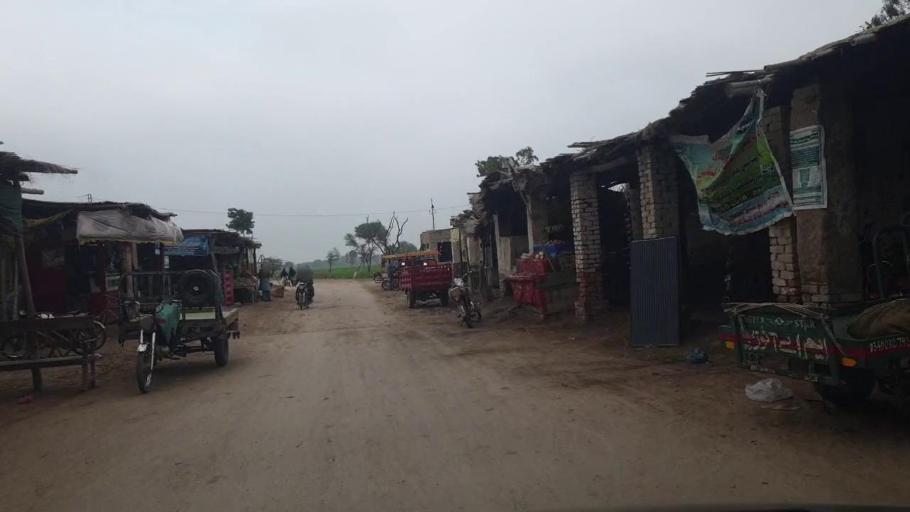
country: PK
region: Sindh
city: Shahdadpur
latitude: 25.9373
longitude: 68.7259
